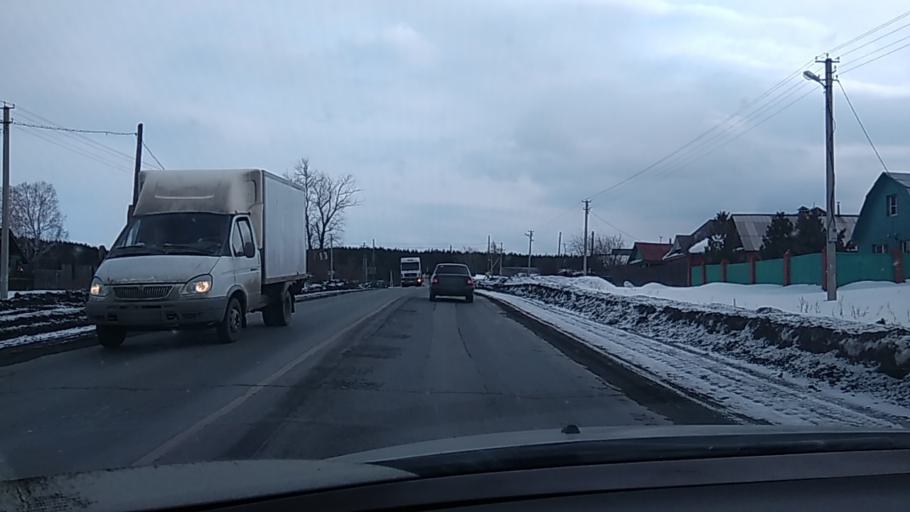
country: RU
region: Sverdlovsk
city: Dvurechensk
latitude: 56.6352
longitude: 61.2575
